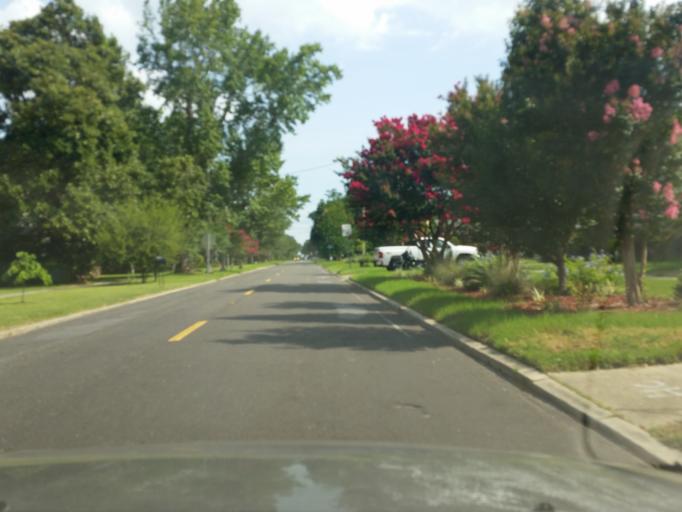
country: US
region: Florida
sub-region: Escambia County
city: Pensacola
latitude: 30.4324
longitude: -87.2046
